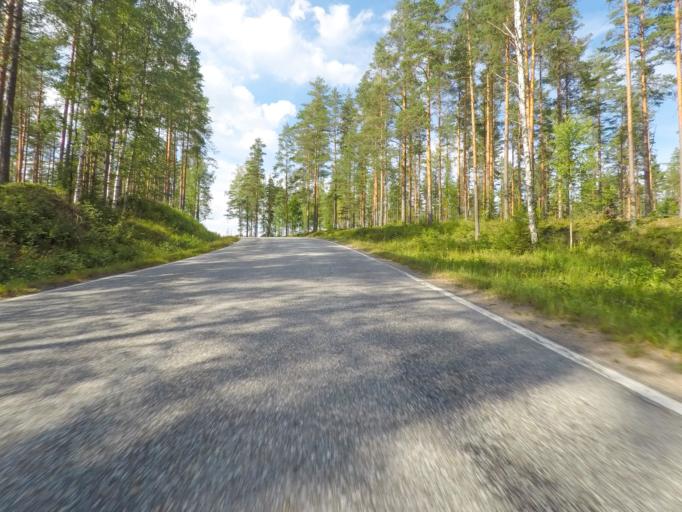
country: FI
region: Southern Savonia
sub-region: Mikkeli
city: Puumala
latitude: 61.6955
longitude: 28.2159
